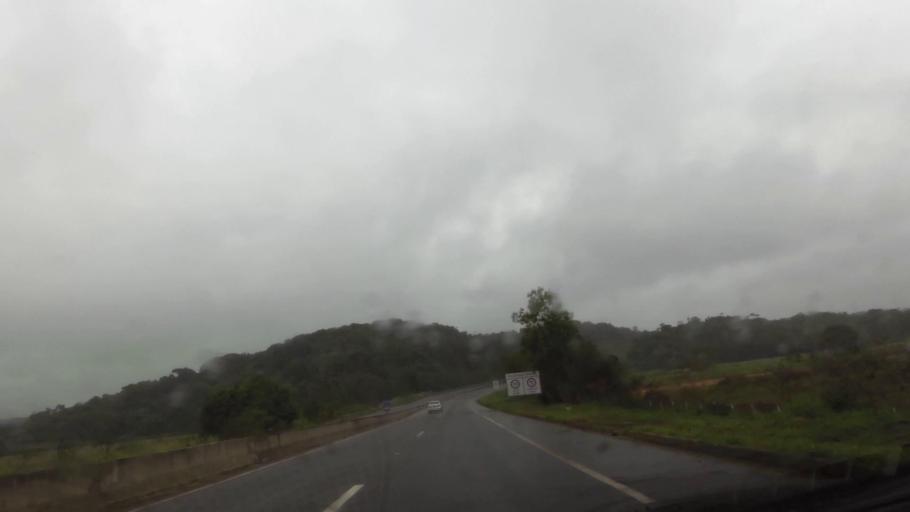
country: BR
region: Espirito Santo
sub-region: Guarapari
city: Guarapari
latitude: -20.6150
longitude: -40.4918
